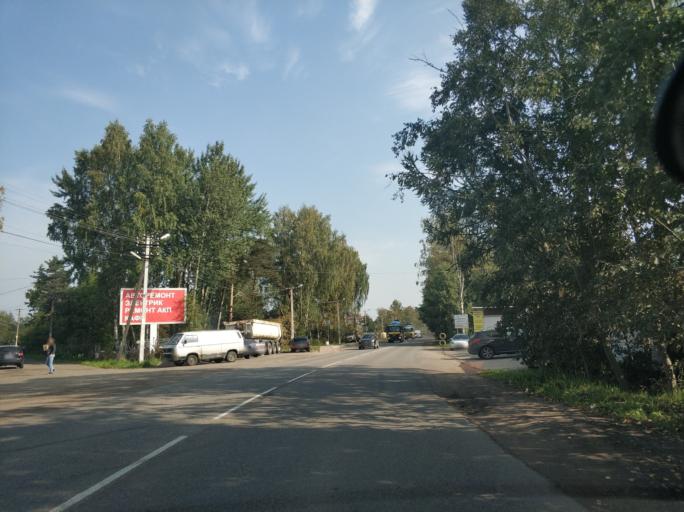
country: RU
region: Leningrad
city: Vsevolozhsk
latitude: 60.0175
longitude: 30.6252
